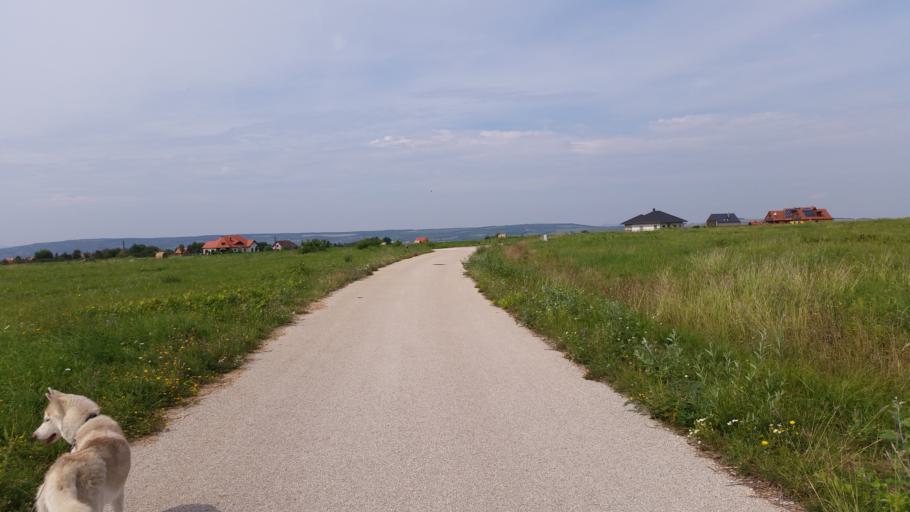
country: HU
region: Pest
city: Telki
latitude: 47.5609
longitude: 18.8102
